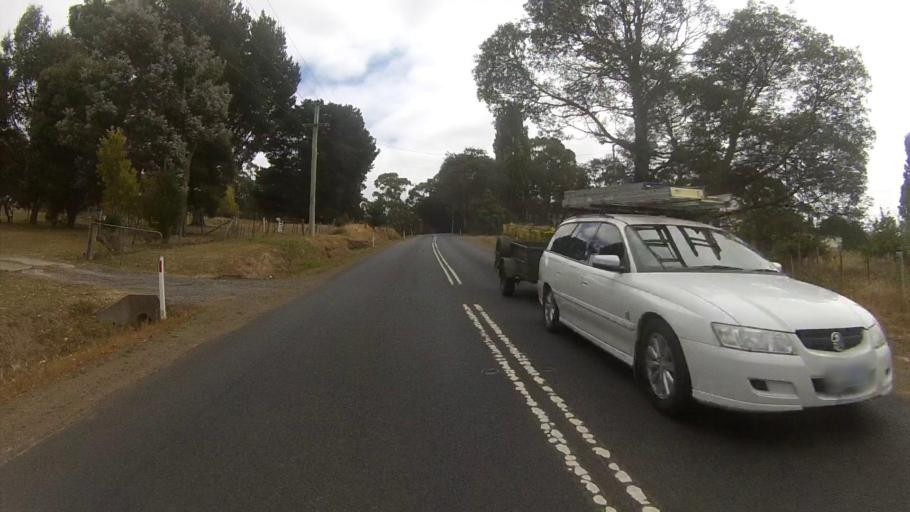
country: AU
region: Tasmania
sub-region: Kingborough
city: Margate
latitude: -43.0204
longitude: 147.2537
